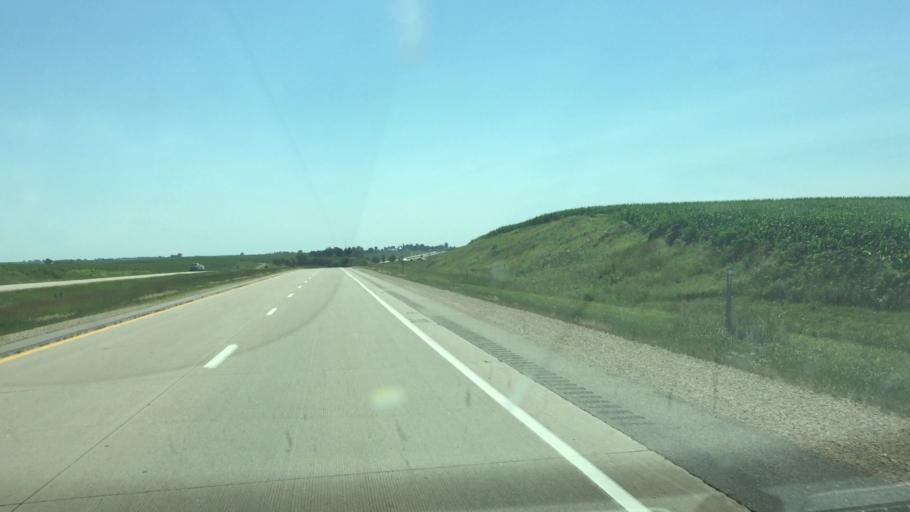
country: US
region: Iowa
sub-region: Dubuque County
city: Peosta
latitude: 42.3529
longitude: -90.8244
